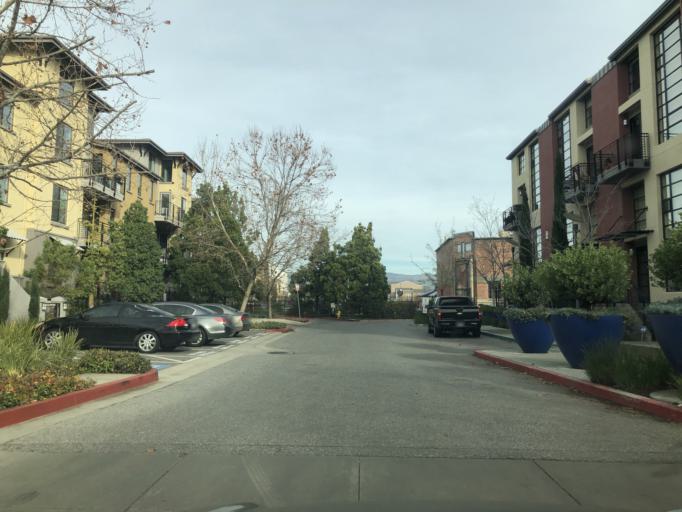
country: US
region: California
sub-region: Santa Clara County
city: San Jose
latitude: 37.3548
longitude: -121.8944
